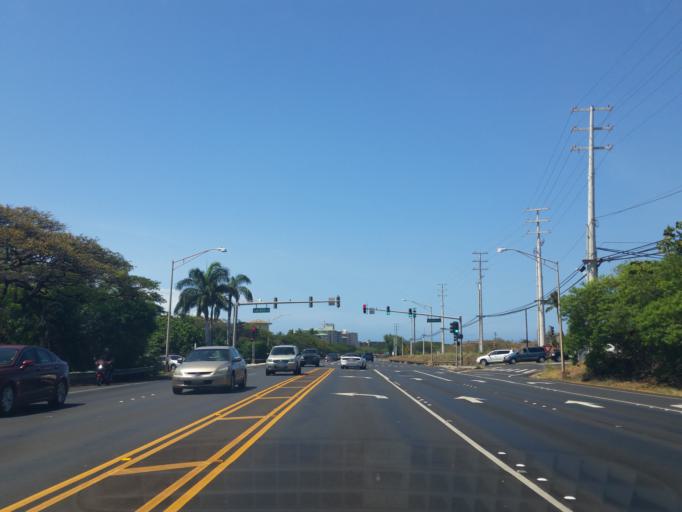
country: US
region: Hawaii
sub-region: Maui County
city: Kaanapali Landing
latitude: 20.9353
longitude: -156.6901
